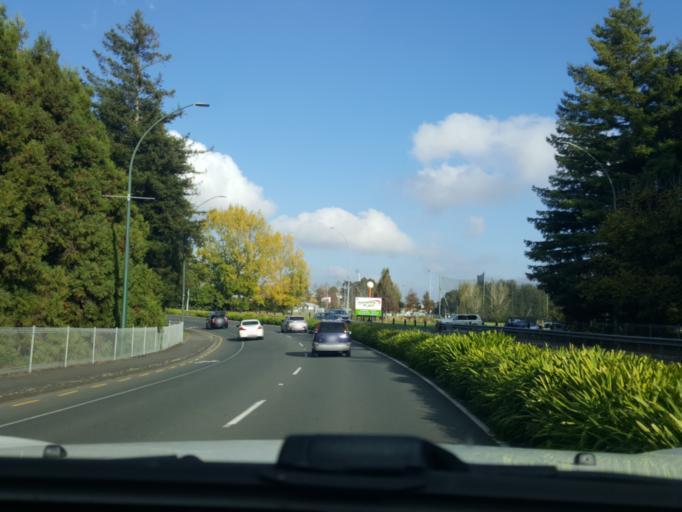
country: NZ
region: Waikato
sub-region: Hamilton City
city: Hamilton
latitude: -37.7746
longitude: 175.2646
